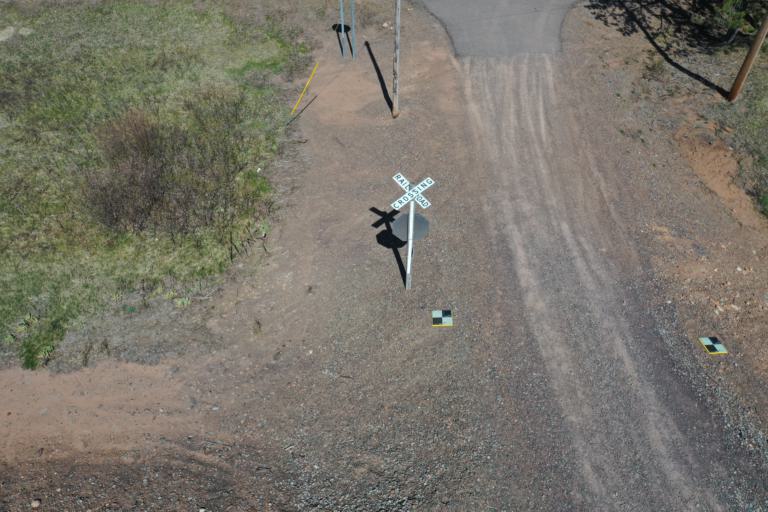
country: US
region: Minnesota
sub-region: Carlton County
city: Moose Lake
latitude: 46.4001
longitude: -92.5120
